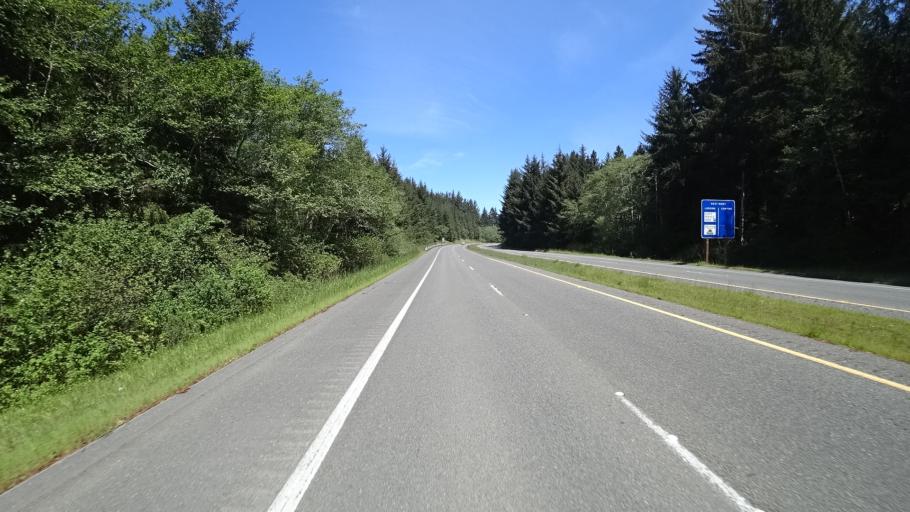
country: US
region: California
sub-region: Humboldt County
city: Westhaven-Moonstone
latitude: 41.1300
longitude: -124.1506
